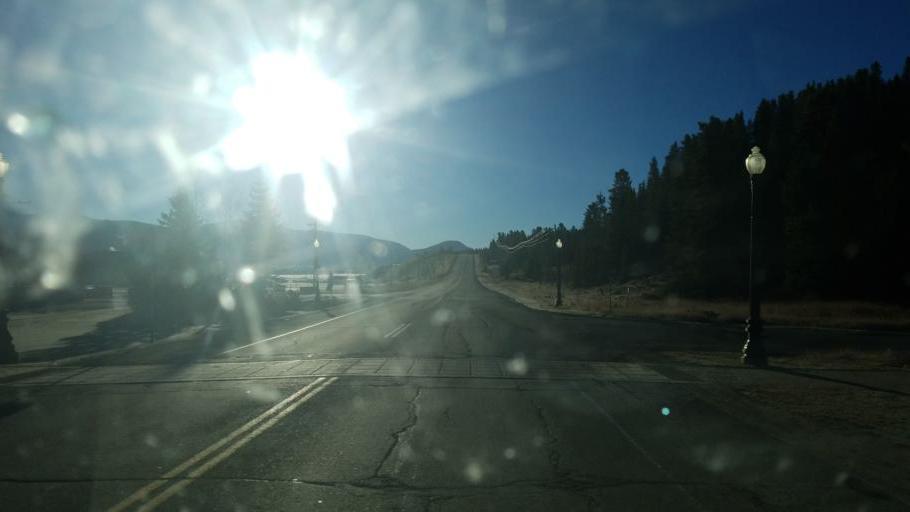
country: US
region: Colorado
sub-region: Gunnison County
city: Crested Butte
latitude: 38.8666
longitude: -106.9797
